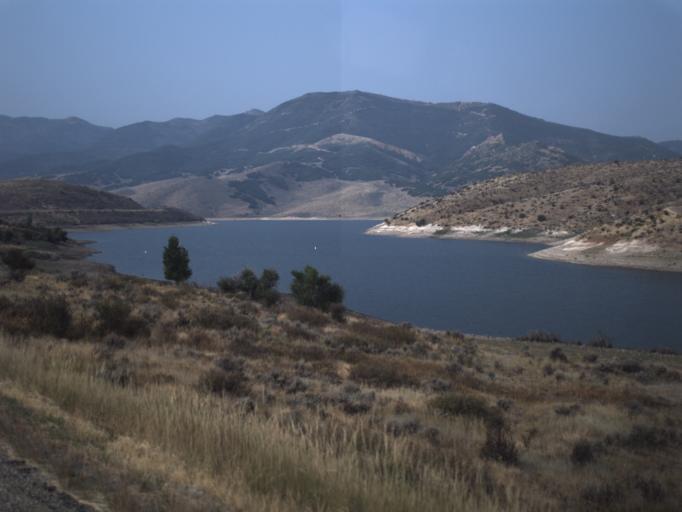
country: US
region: Utah
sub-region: Morgan County
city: Morgan
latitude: 40.9207
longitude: -111.5761
